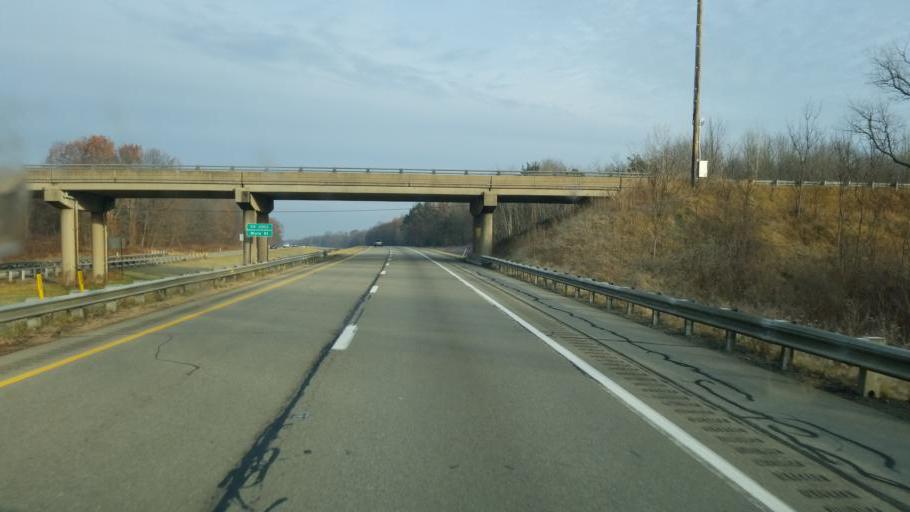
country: US
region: Pennsylvania
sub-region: Crawford County
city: Cochranton
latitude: 41.4909
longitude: -80.1664
